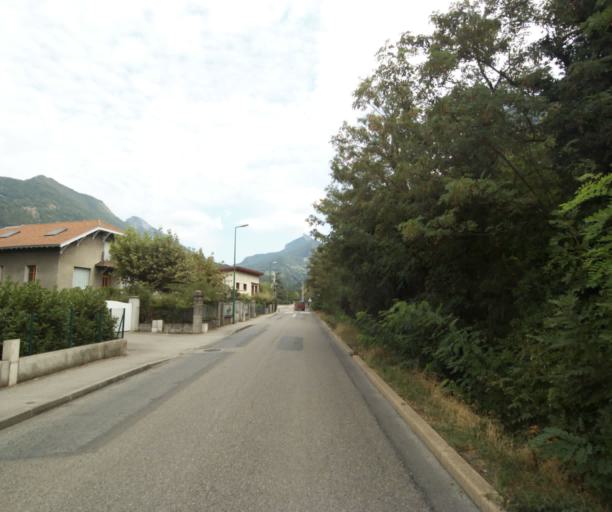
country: FR
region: Rhone-Alpes
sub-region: Departement de l'Isere
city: Saint-Egreve
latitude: 45.2321
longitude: 5.6850
